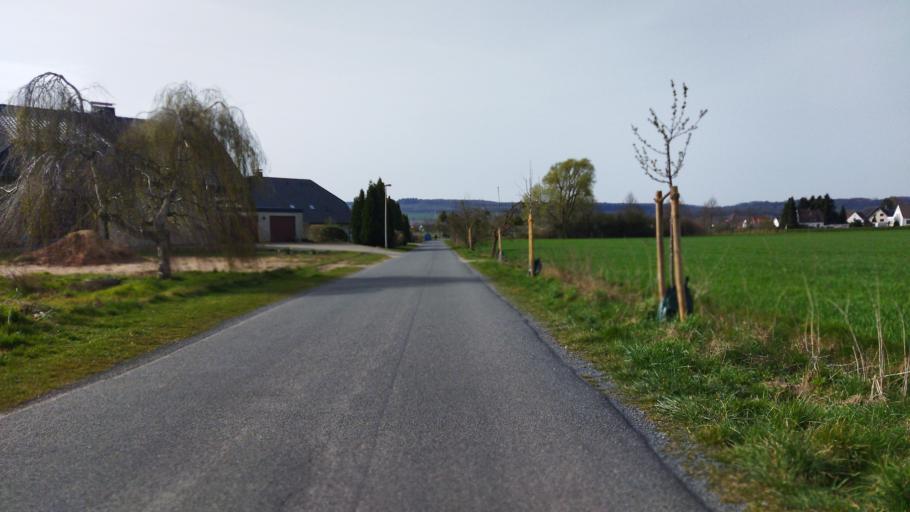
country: DE
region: North Rhine-Westphalia
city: Porta Westfalica
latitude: 52.1977
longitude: 8.9802
